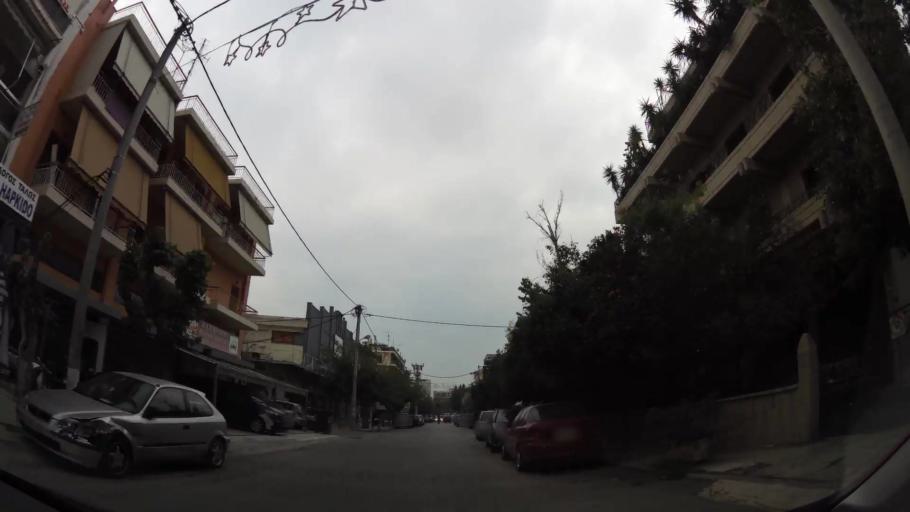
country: GR
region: Attica
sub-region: Nomarchia Athinas
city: Peristeri
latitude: 38.0029
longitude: 23.6879
